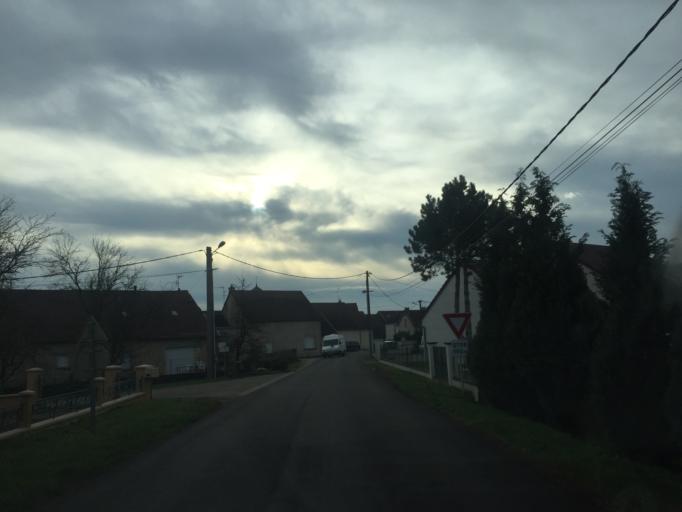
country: FR
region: Franche-Comte
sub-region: Departement du Jura
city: Tavaux
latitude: 47.0214
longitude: 5.4181
